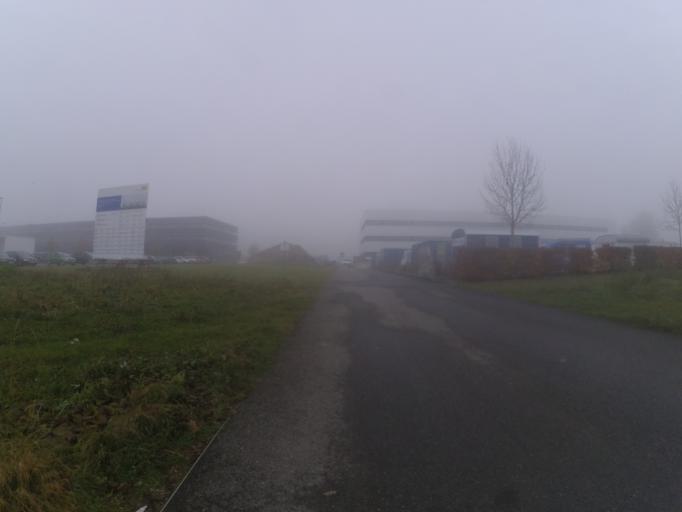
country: DE
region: Bavaria
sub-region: Swabia
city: Neu-Ulm
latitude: 48.3798
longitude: 10.0108
